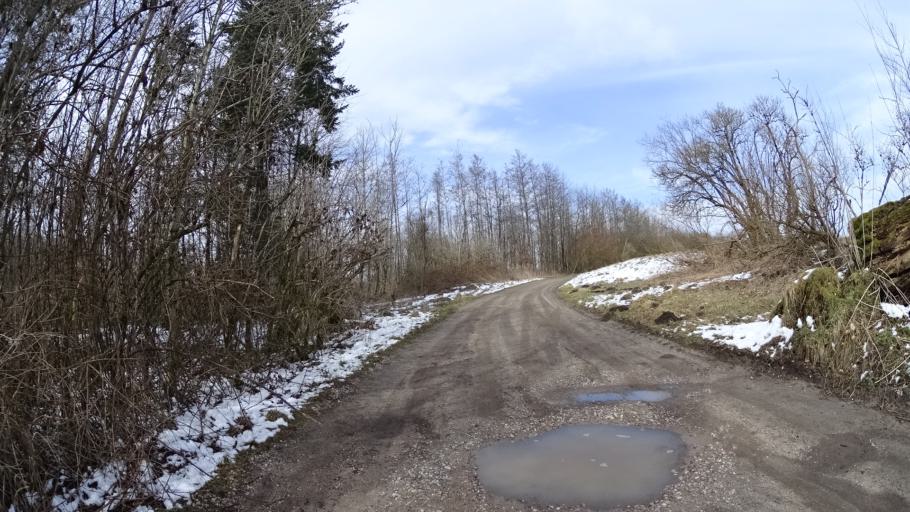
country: DE
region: Schleswig-Holstein
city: Loptin
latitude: 54.1643
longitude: 10.2280
